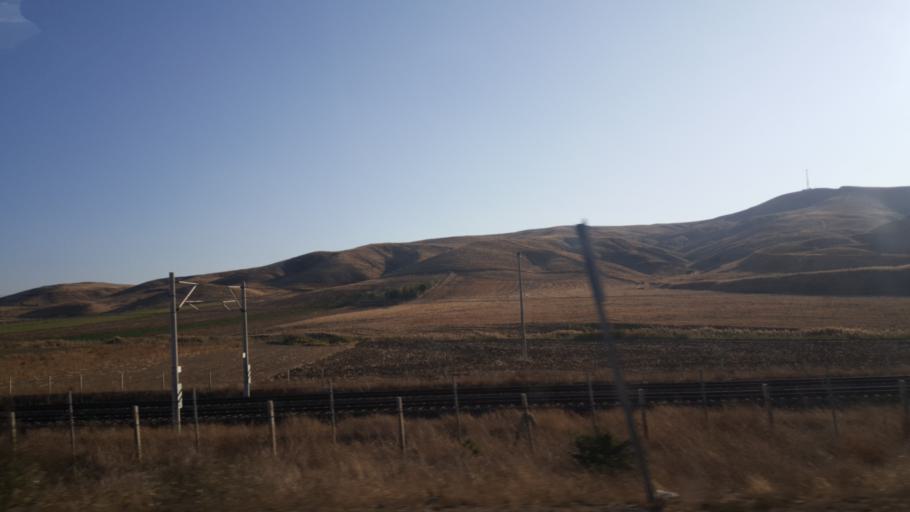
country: TR
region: Ankara
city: Polatli
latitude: 39.5744
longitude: 32.0782
